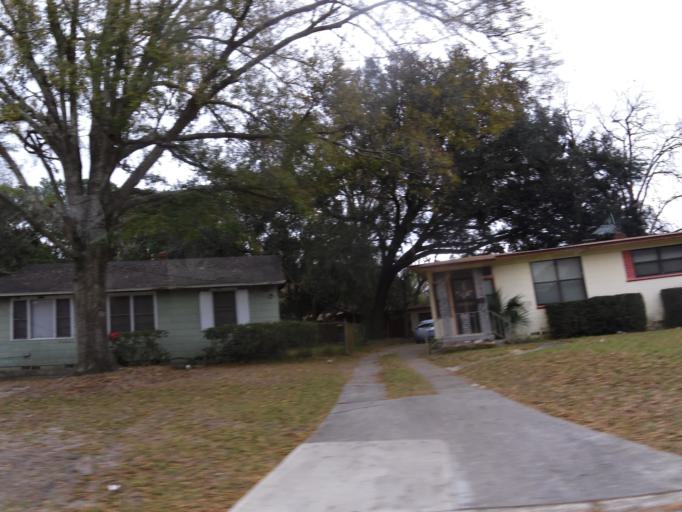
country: US
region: Florida
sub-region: Duval County
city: Jacksonville
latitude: 30.3670
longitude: -81.7053
